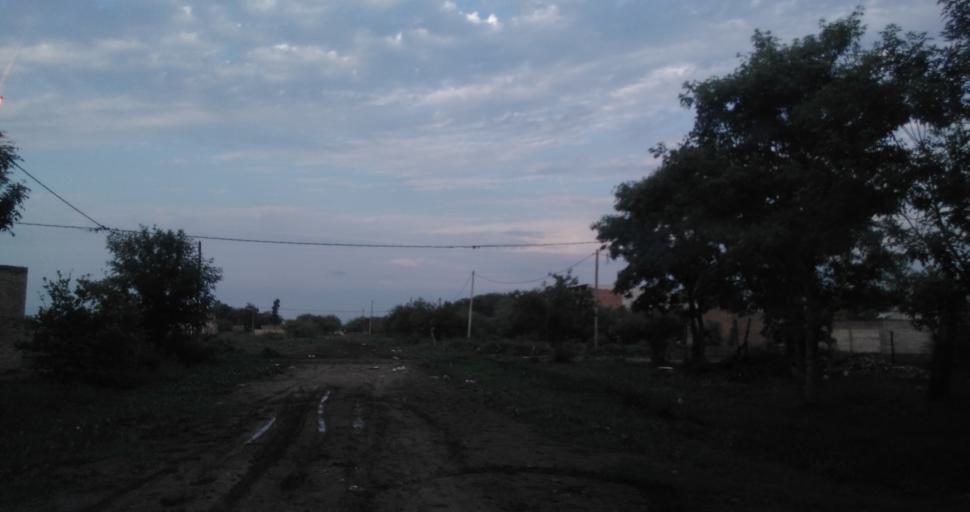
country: AR
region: Chaco
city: Resistencia
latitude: -27.4827
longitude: -59.0040
